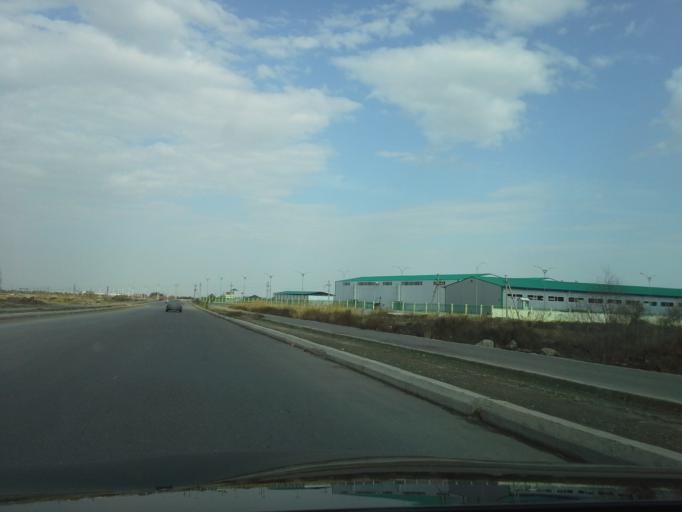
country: TM
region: Ahal
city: Abadan
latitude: 37.9898
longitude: 58.2765
